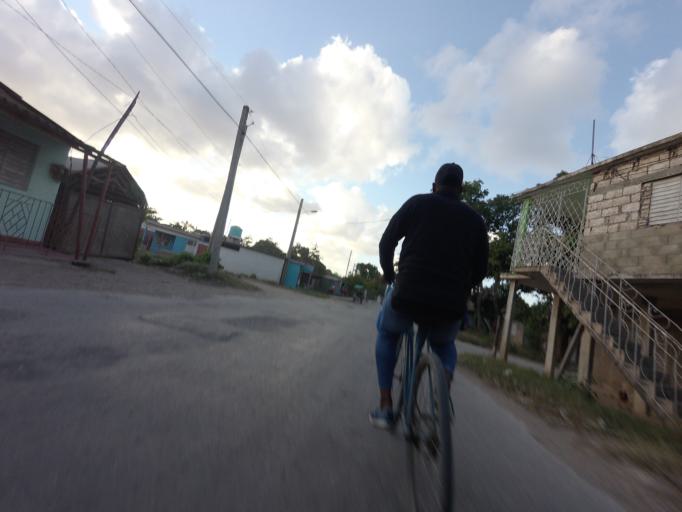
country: CU
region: Ciego de Avila
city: Ciego de Avila
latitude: 21.8319
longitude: -78.7566
